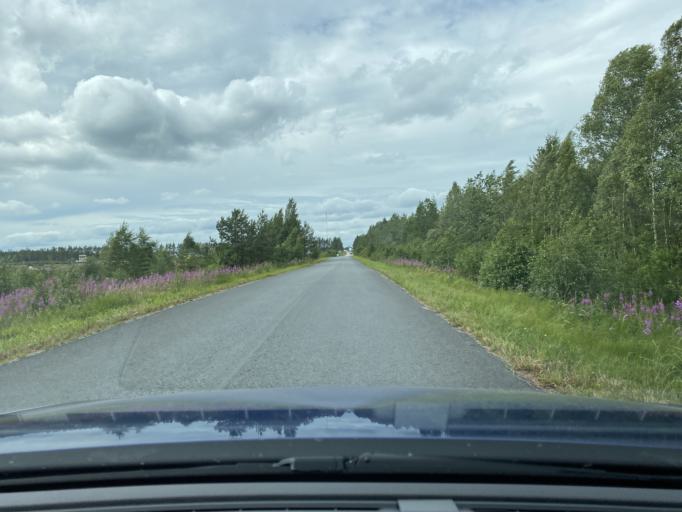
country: FI
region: Southern Ostrobothnia
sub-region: Seinaejoki
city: Jurva
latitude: 62.6266
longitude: 22.0262
